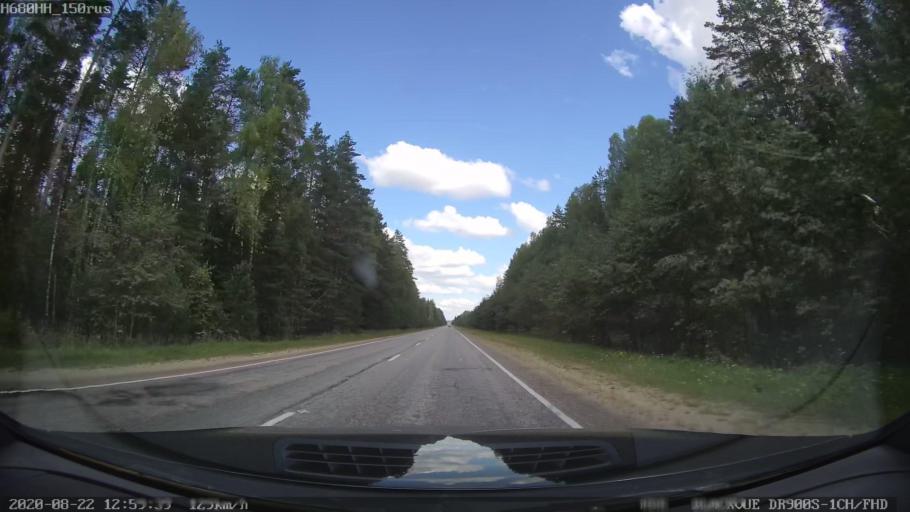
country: RU
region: Tverskaya
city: Bezhetsk
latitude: 57.6098
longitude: 36.3632
